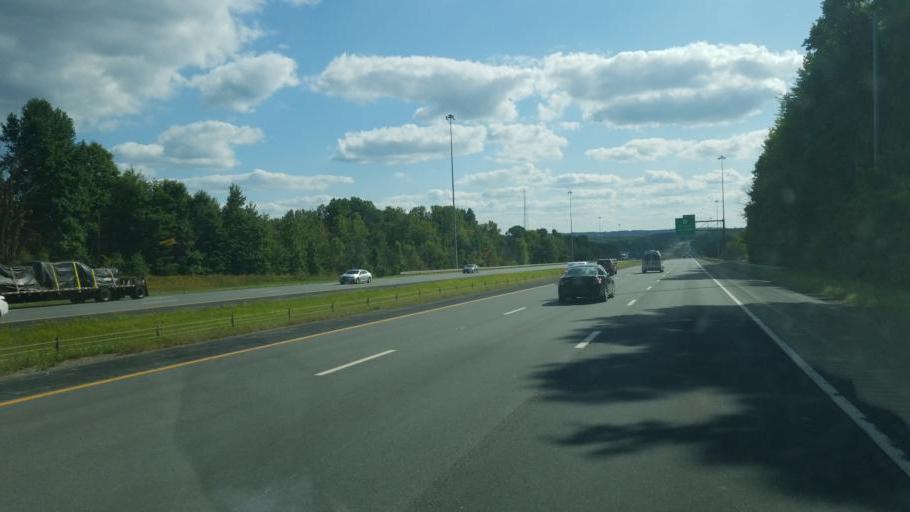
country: US
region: Ohio
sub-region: Richland County
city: Lexington
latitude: 40.6599
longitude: -82.5400
